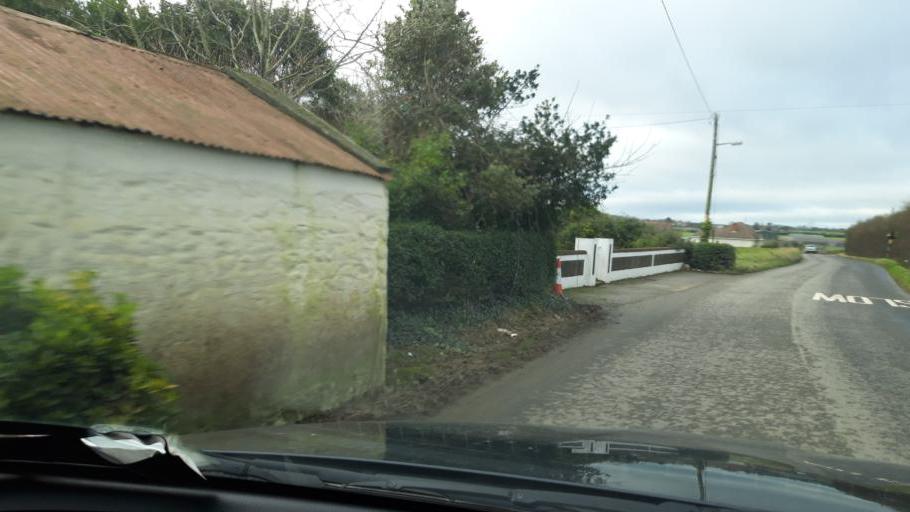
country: IE
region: Leinster
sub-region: Fingal County
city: Skerries
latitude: 53.5560
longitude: -6.1319
